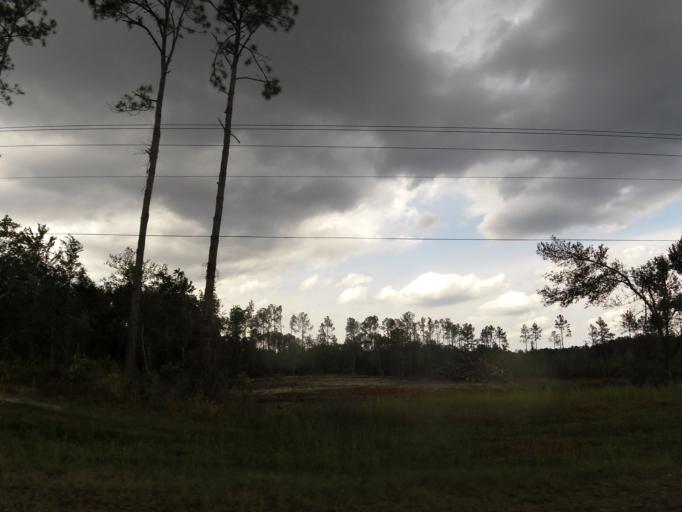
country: US
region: Georgia
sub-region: Charlton County
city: Folkston
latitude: 30.8408
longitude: -81.9739
